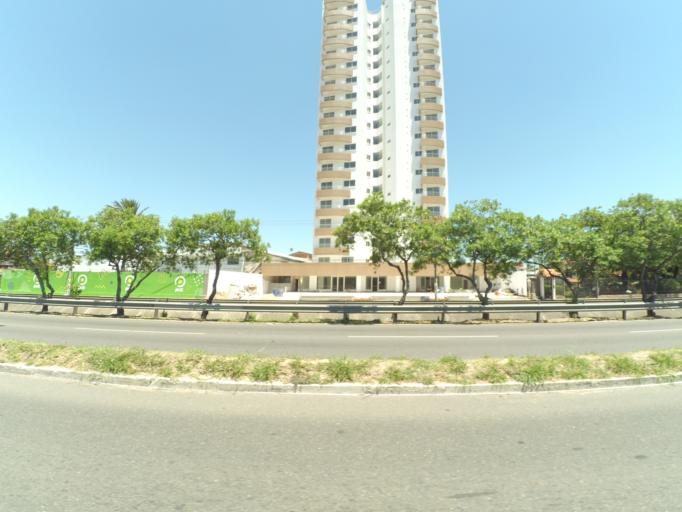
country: BO
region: Santa Cruz
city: Santa Cruz de la Sierra
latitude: -17.7814
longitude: -63.1941
